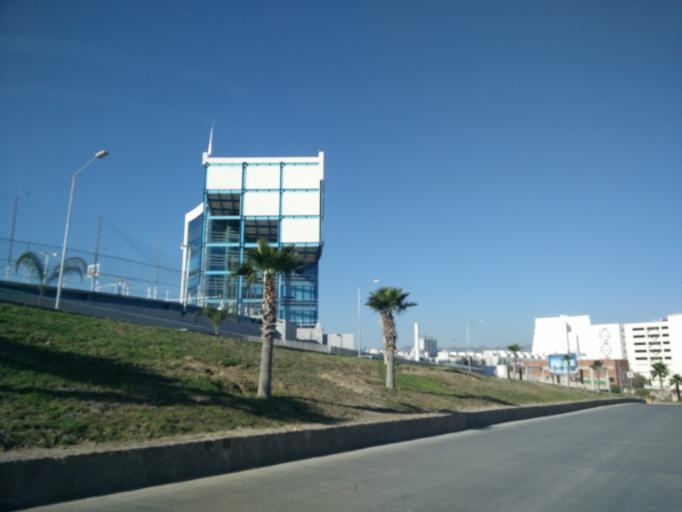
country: MX
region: San Luis Potosi
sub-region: San Luis Potosi
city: San Luis Potosi
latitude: 22.1208
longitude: -101.0187
